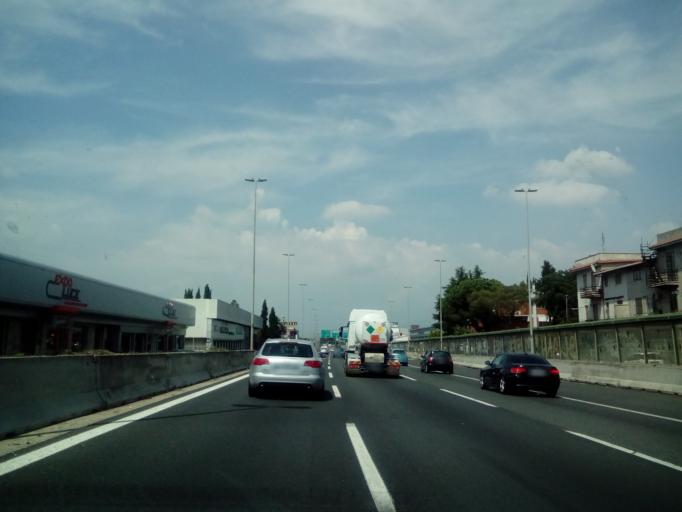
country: IT
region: Latium
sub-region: Citta metropolitana di Roma Capitale
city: Ciampino
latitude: 41.8296
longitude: 12.5850
